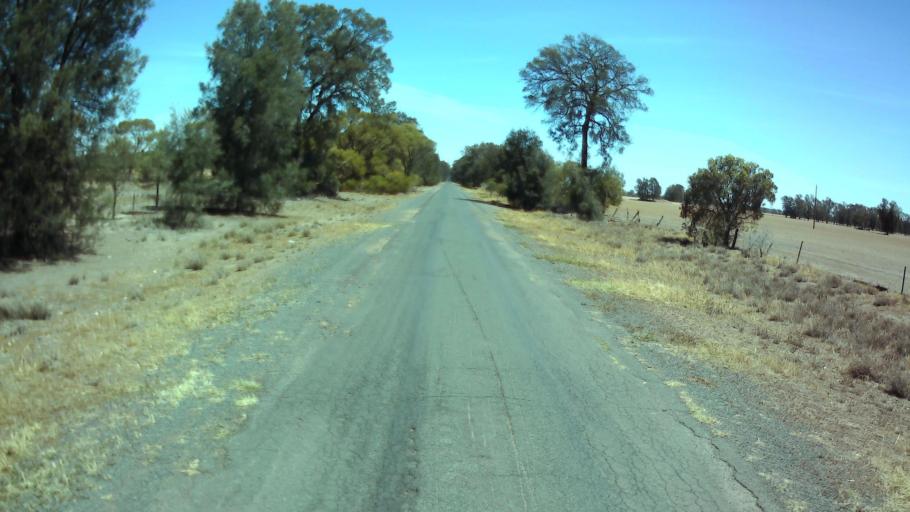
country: AU
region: New South Wales
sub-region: Weddin
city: Grenfell
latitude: -33.8746
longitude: 147.6914
